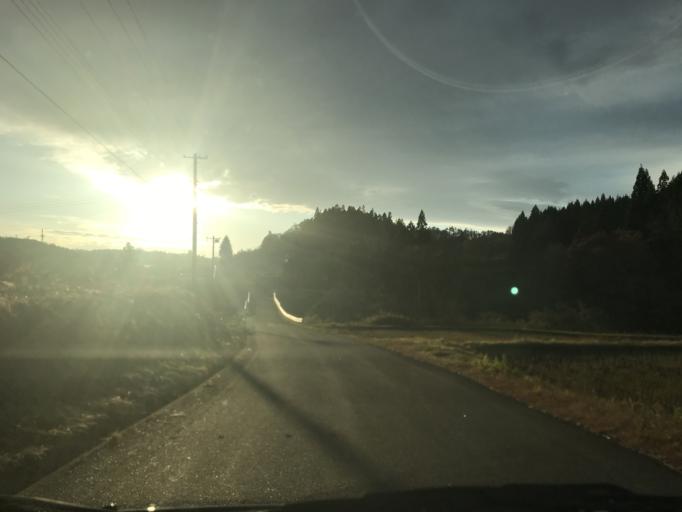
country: JP
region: Iwate
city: Ichinoseki
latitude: 38.9990
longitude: 141.0707
